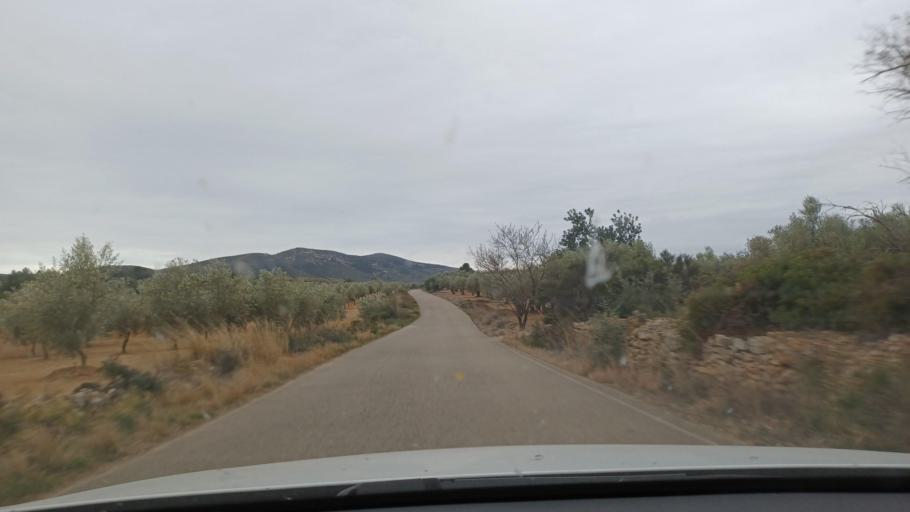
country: ES
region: Valencia
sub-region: Provincia de Castello
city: Canet lo Roig
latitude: 40.5709
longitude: 0.2763
